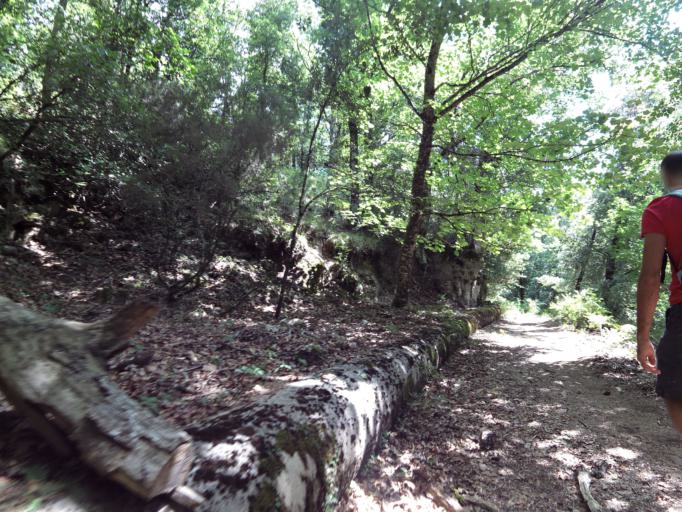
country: IT
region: Calabria
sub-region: Provincia di Vibo-Valentia
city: Nardodipace
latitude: 38.5078
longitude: 16.3848
